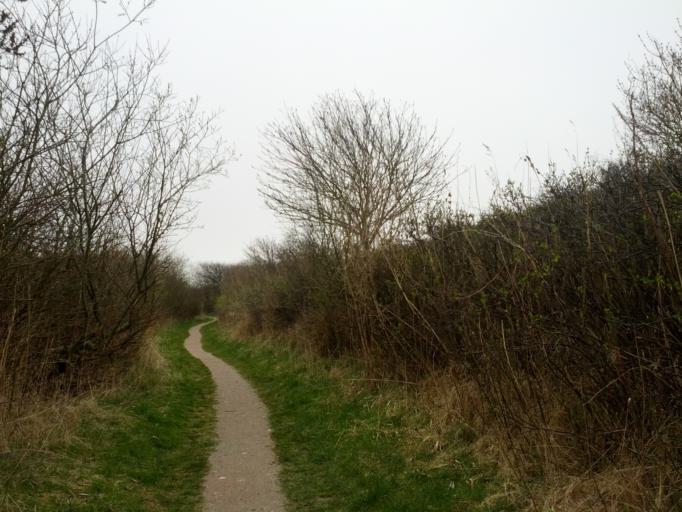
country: DE
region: Lower Saxony
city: Langeoog
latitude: 53.7389
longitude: 7.4714
